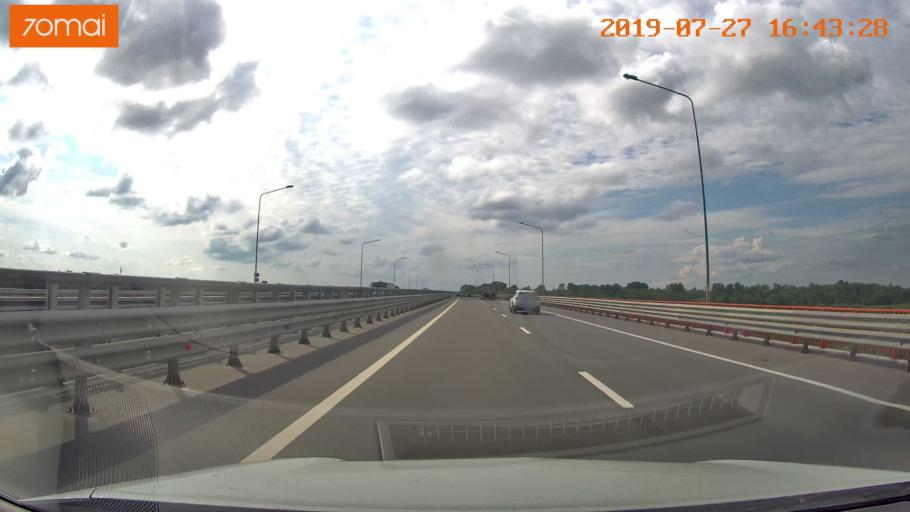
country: RU
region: Kaliningrad
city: Gvardeysk
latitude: 54.6714
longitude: 21.1017
